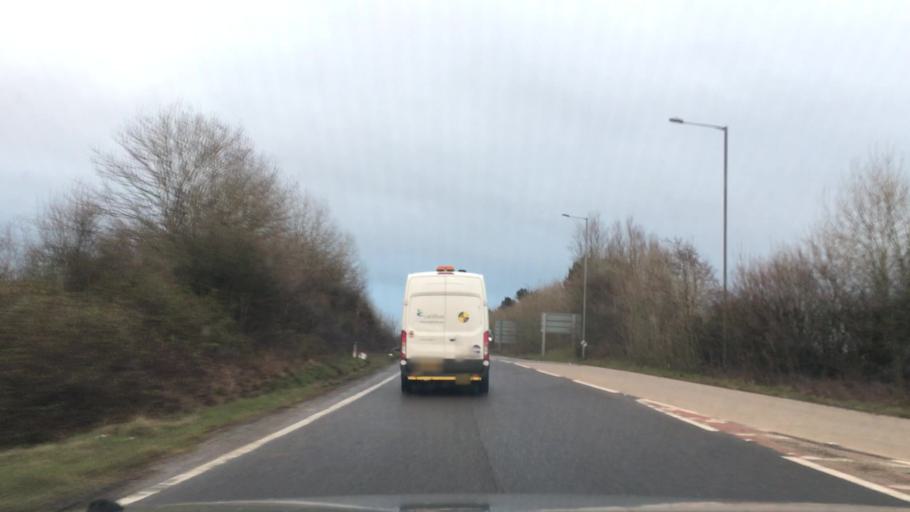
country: GB
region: England
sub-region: Cumbria
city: Dalton in Furness
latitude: 54.1638
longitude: -3.1879
